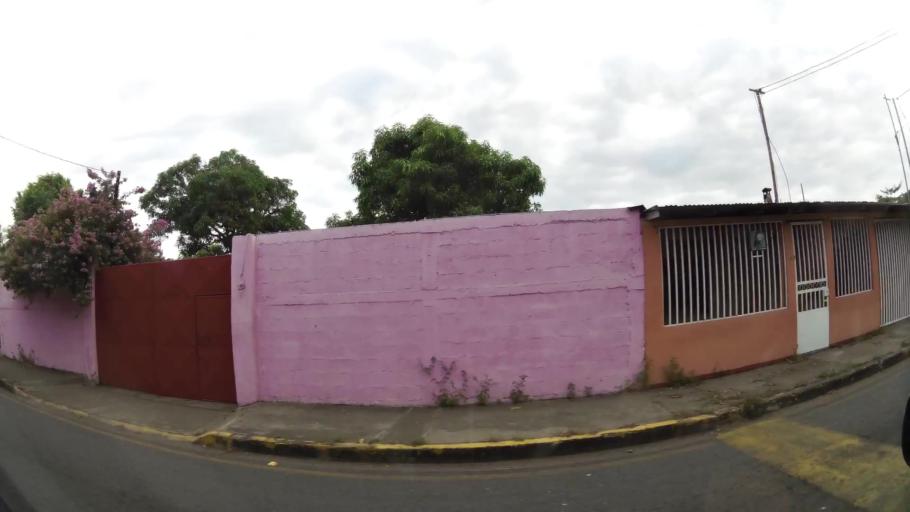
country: CR
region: Puntarenas
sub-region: Canton Central de Puntarenas
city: Chacarita
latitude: 9.9814
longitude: -84.8040
